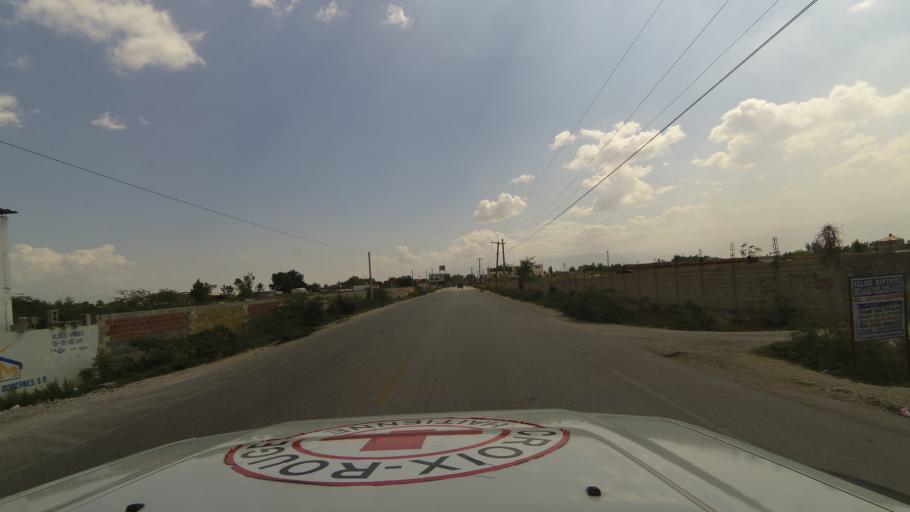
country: HT
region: Ouest
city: Croix des Bouquets
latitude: 18.6420
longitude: -72.2726
